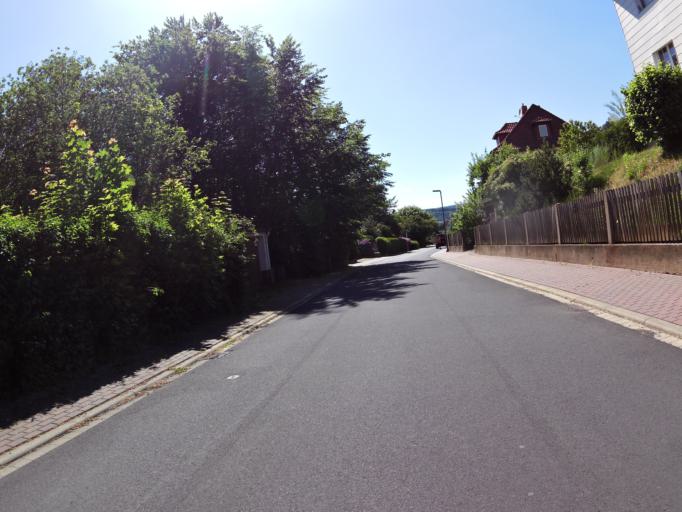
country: DE
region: Hesse
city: Philippsthal
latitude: 50.8427
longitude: 10.0015
